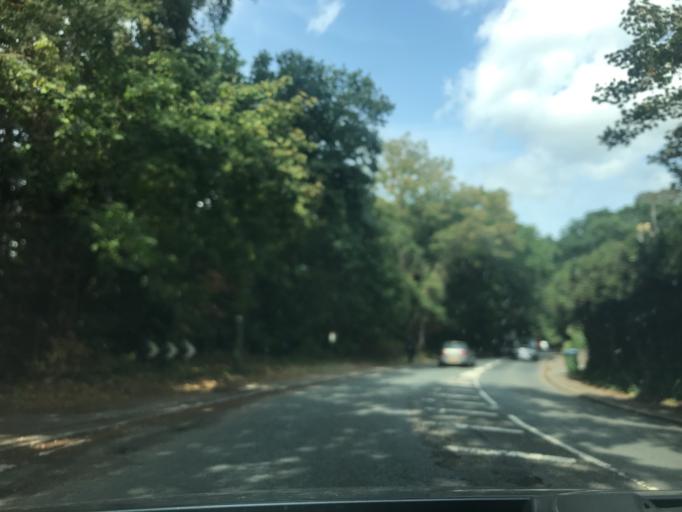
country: GB
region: England
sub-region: Surrey
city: Weybridge
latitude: 51.3589
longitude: -0.4572
